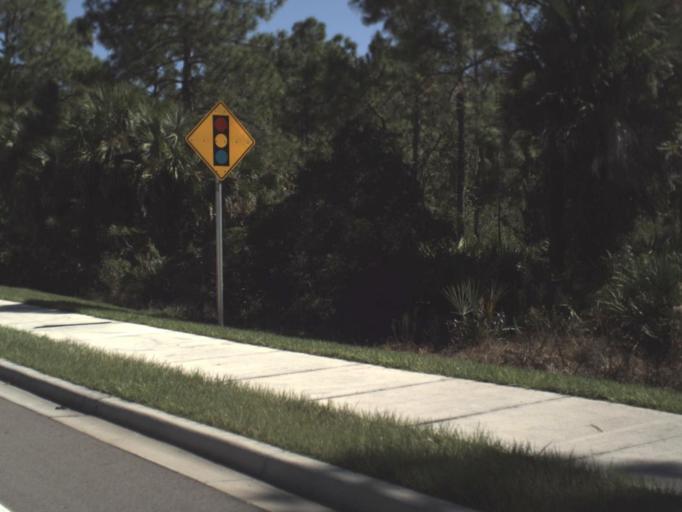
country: US
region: Florida
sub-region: Collier County
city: Golden Gate
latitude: 26.1515
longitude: -81.6995
